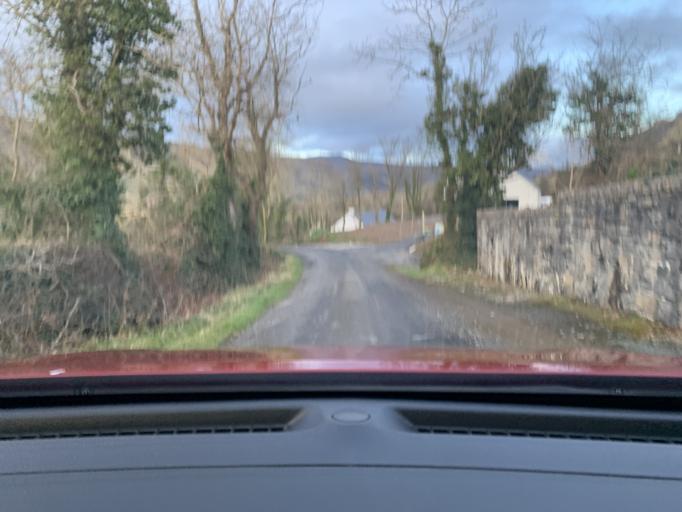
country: IE
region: Connaught
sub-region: Sligo
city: Sligo
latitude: 54.3137
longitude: -8.4503
